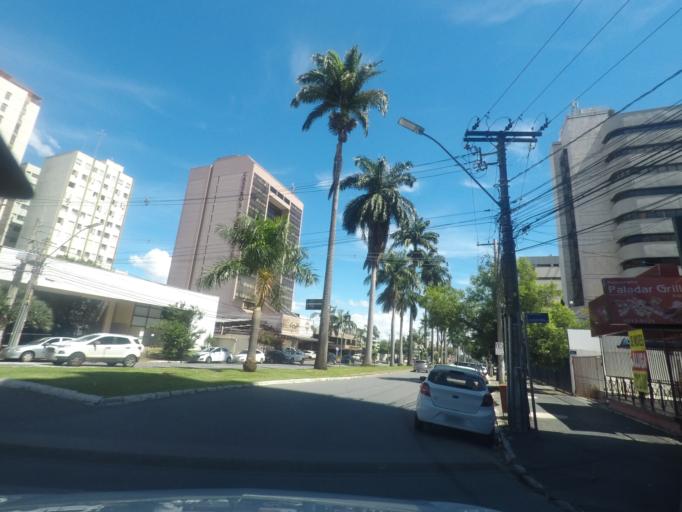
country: BR
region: Goias
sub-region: Goiania
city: Goiania
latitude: -16.6800
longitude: -49.2668
